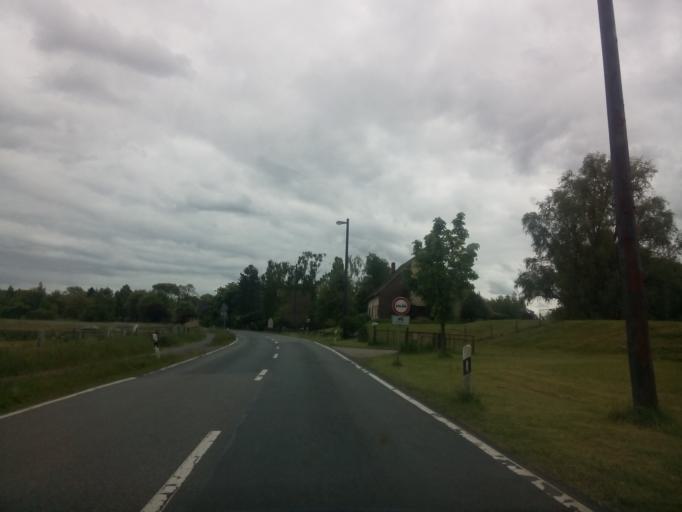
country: DE
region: Lower Saxony
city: Delmenhorst
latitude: 53.0926
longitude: 8.6681
